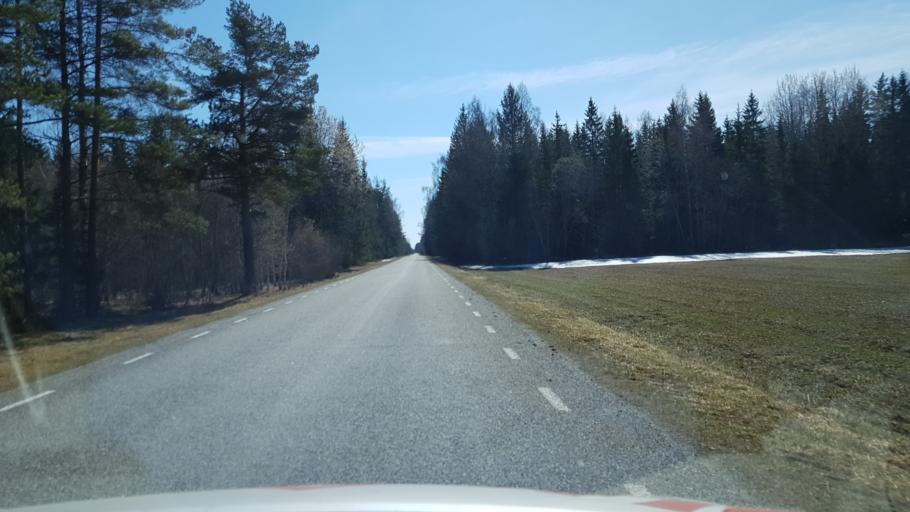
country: EE
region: Laeaene-Virumaa
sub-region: Vinni vald
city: Vinni
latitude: 59.1717
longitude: 26.5068
